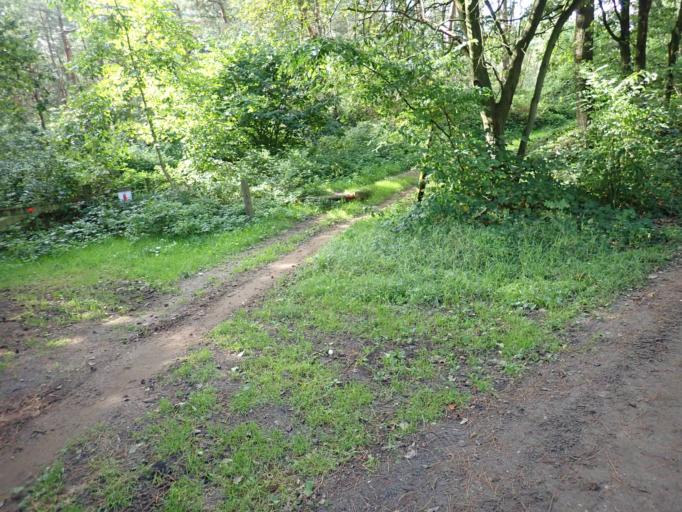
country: BE
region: Flanders
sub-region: Provincie Antwerpen
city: Lille
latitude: 51.2769
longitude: 4.8044
